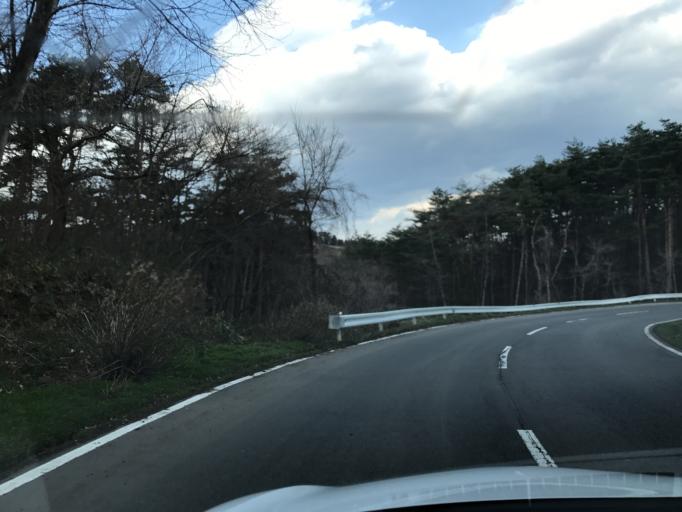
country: JP
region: Miyagi
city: Shiroishi
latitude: 38.0241
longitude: 140.5590
